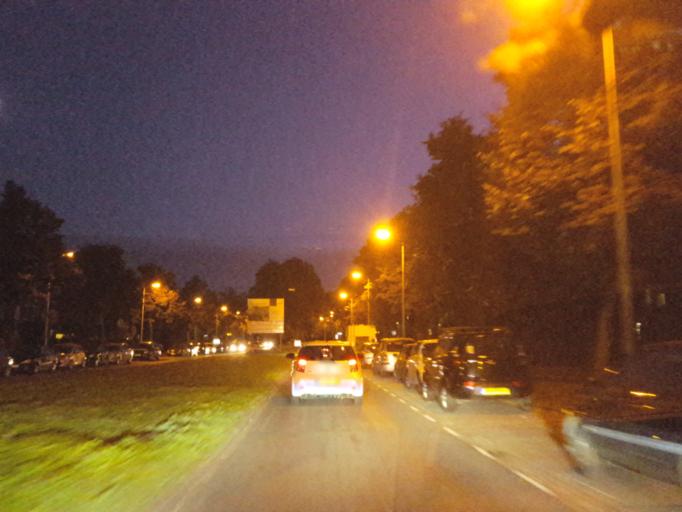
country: NL
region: Utrecht
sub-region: Gemeente Utrecht
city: Utrecht
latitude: 52.0919
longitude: 5.0839
